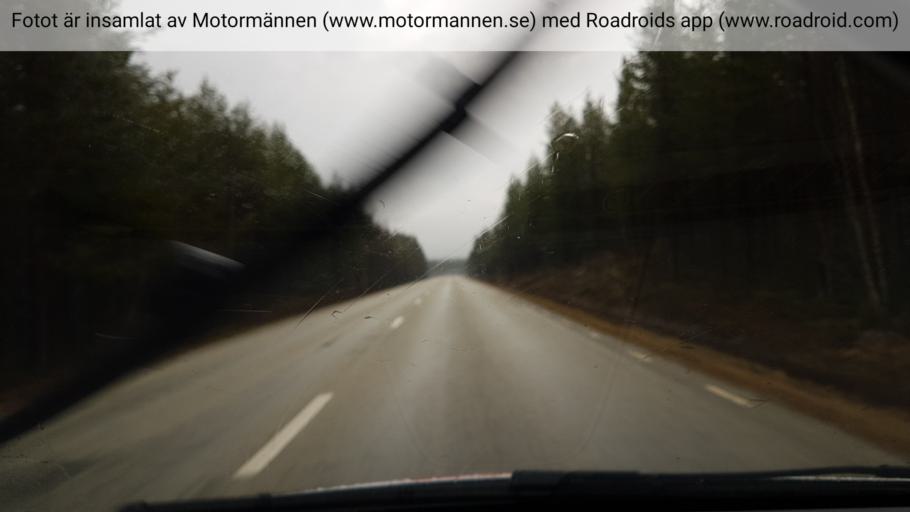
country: SE
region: Jaemtland
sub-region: Harjedalens Kommun
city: Sveg
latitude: 62.4203
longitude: 13.7934
